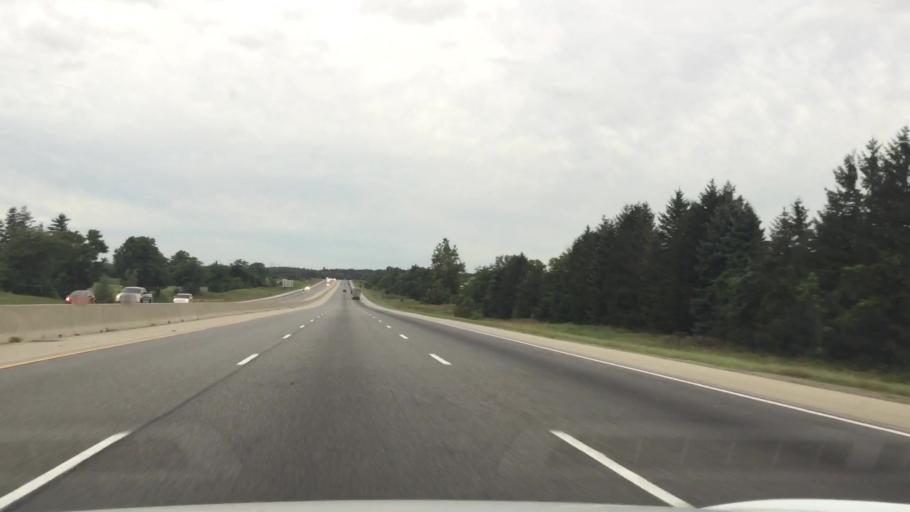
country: CA
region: Ontario
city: Kitchener
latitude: 43.2854
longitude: -80.5123
